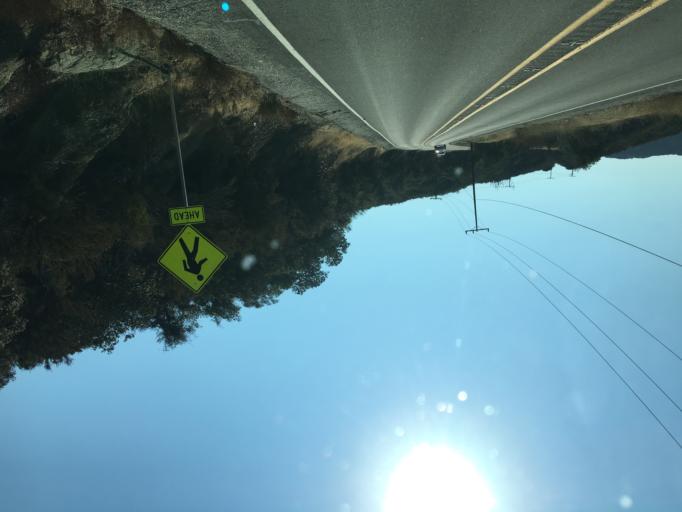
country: US
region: California
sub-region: Los Angeles County
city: Las Flores
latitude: 34.0863
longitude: -118.6613
